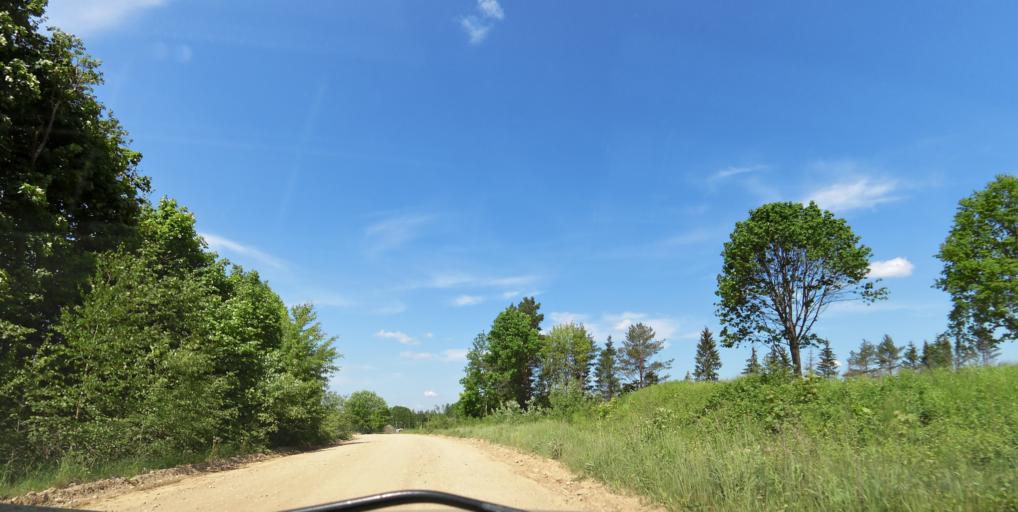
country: LT
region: Vilnius County
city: Pilaite
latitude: 54.7422
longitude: 25.1393
